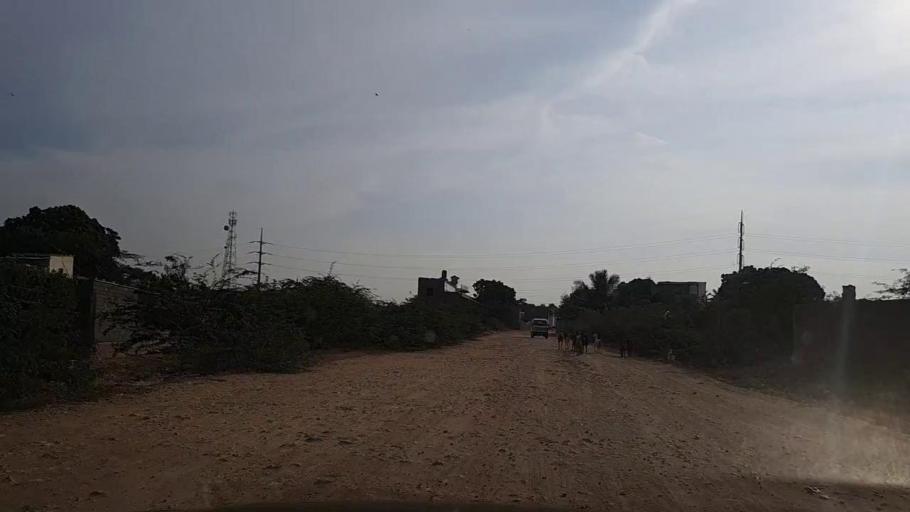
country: PK
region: Sindh
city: Gharo
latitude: 24.7885
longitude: 67.5301
